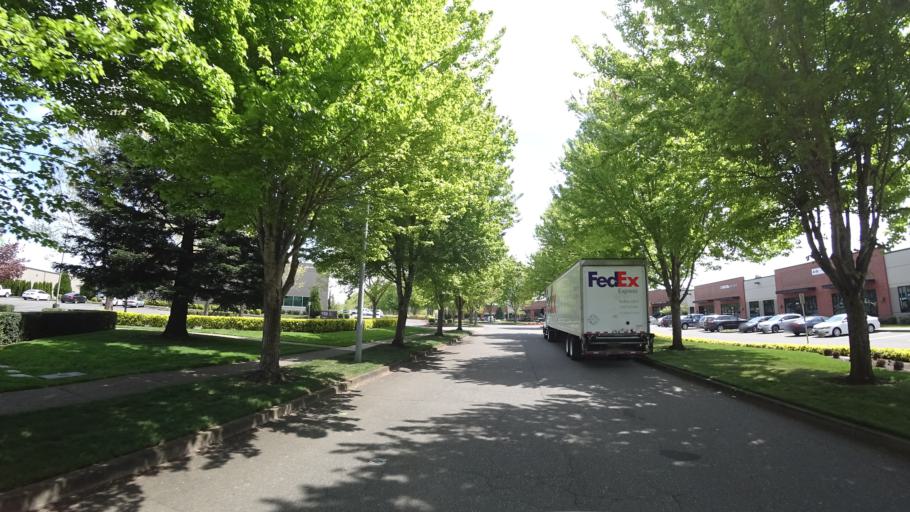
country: US
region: Oregon
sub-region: Washington County
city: Rockcreek
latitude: 45.5641
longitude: -122.9218
